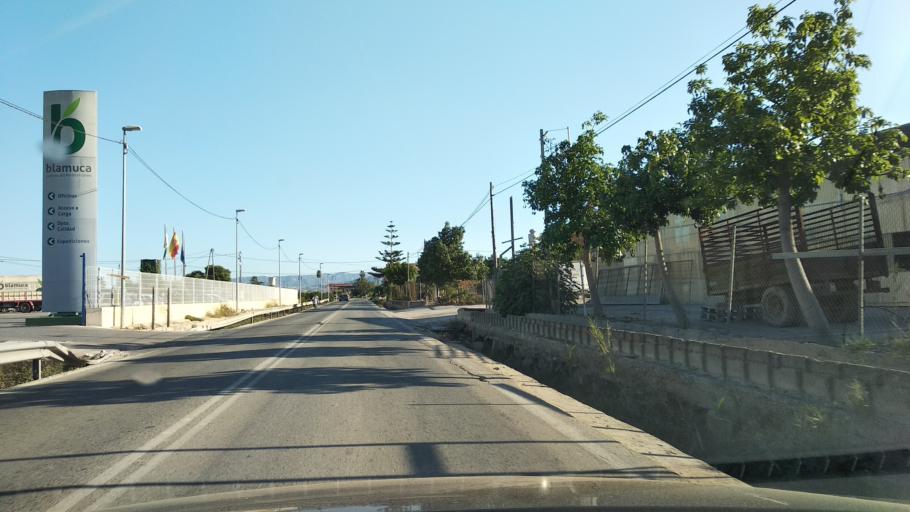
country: ES
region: Murcia
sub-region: Murcia
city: Santomera
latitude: 38.0474
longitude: -1.0545
